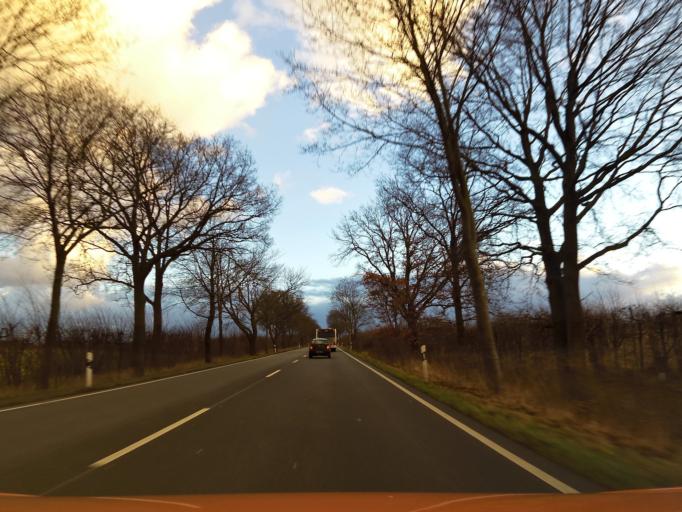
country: DE
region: Lower Saxony
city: Wendeburg
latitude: 52.3543
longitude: 10.4018
